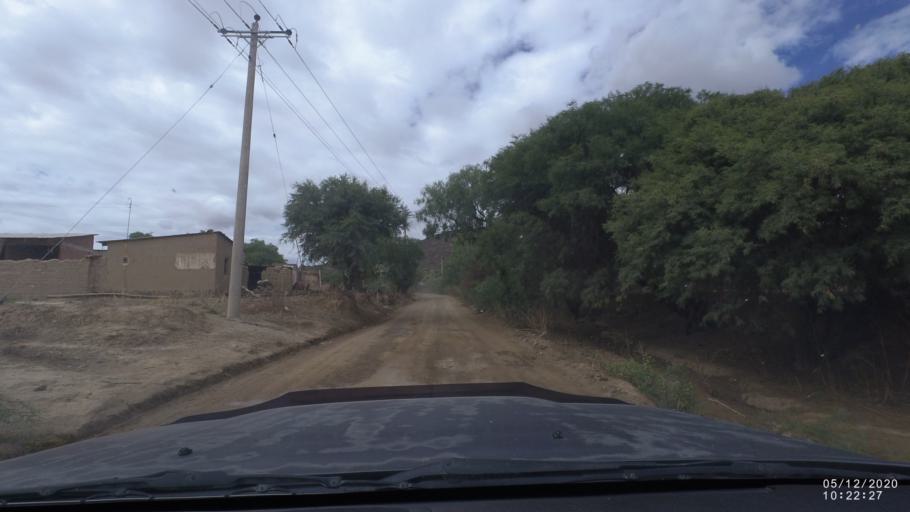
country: BO
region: Cochabamba
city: Sipe Sipe
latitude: -17.4960
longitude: -66.2825
